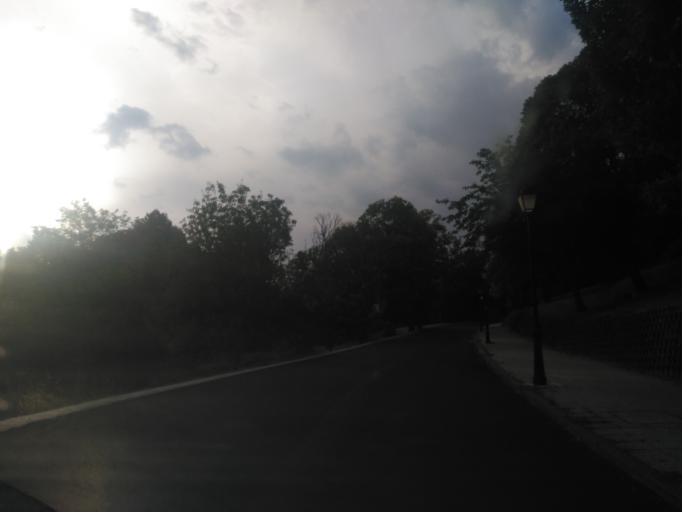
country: ES
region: Castille and Leon
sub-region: Provincia de Salamanca
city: Bejar
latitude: 40.3799
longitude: -5.7646
